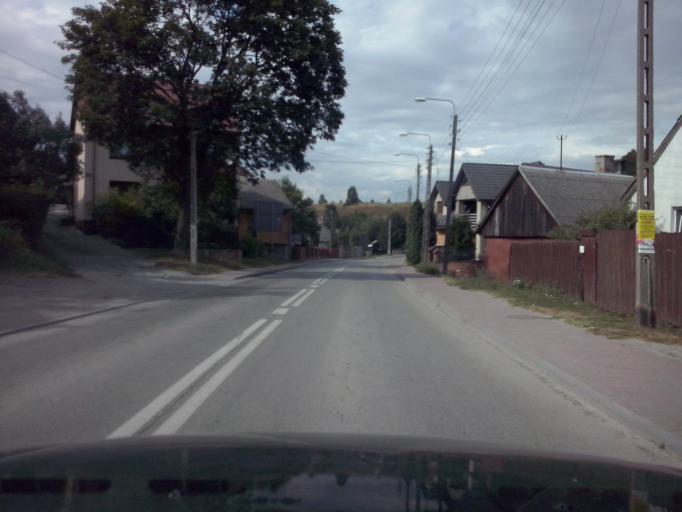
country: PL
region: Swietokrzyskie
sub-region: Powiat kielecki
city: Lagow
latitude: 50.7789
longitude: 21.0850
